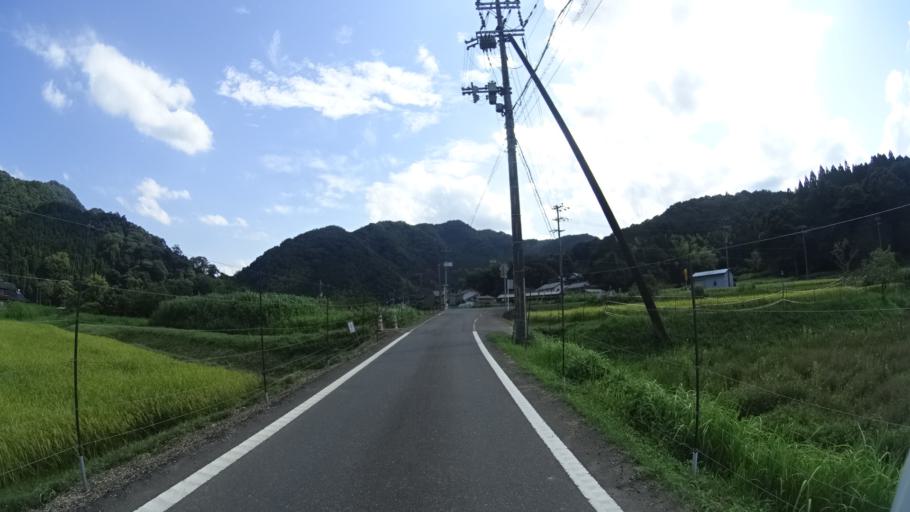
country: JP
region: Kyoto
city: Maizuru
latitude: 35.4316
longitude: 135.2963
